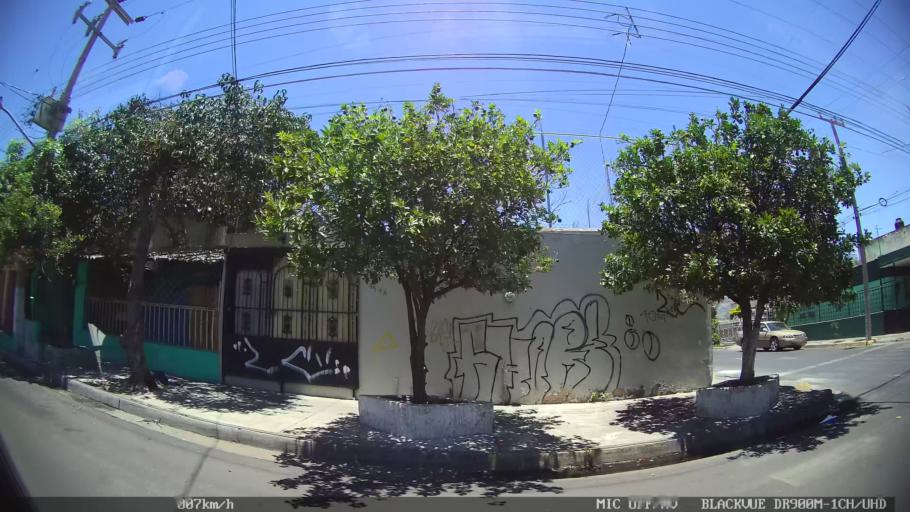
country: MX
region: Jalisco
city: Tlaquepaque
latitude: 20.6758
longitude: -103.2848
